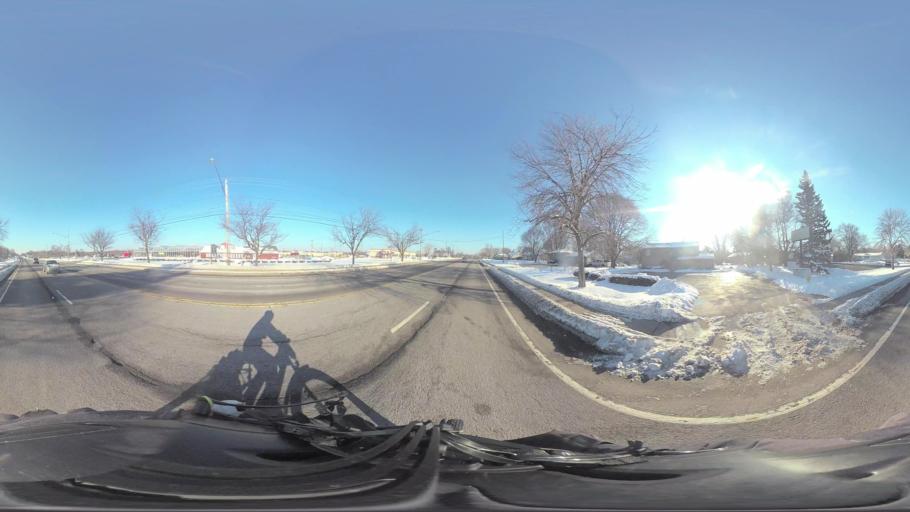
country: US
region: New York
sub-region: Monroe County
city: Rochester
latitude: 43.0652
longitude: -77.6094
